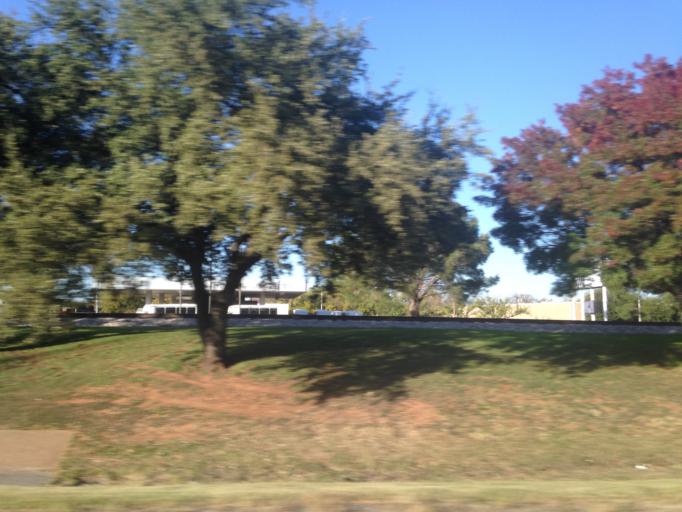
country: US
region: Texas
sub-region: Taylor County
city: Abilene
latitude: 32.4500
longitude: -99.7512
